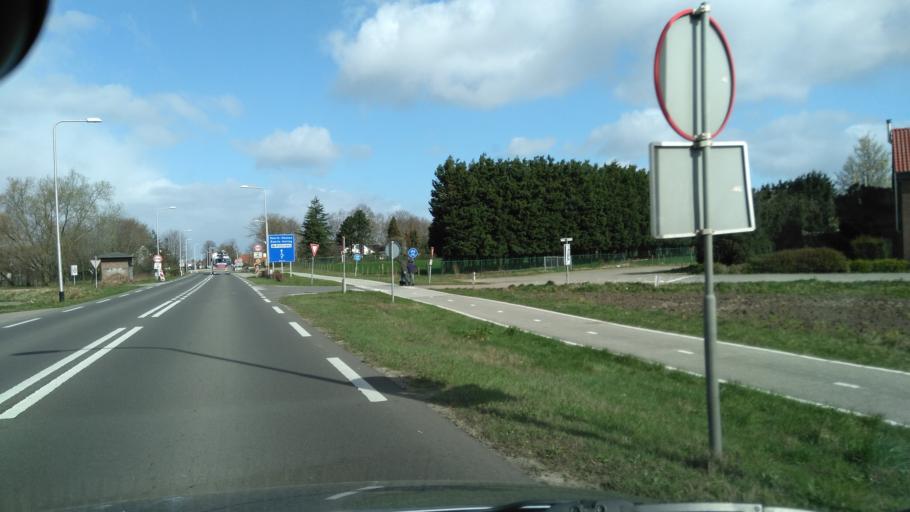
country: NL
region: North Brabant
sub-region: Gemeente Baarle-Nassau
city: Baarle-Nassau
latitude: 51.4263
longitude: 4.9333
